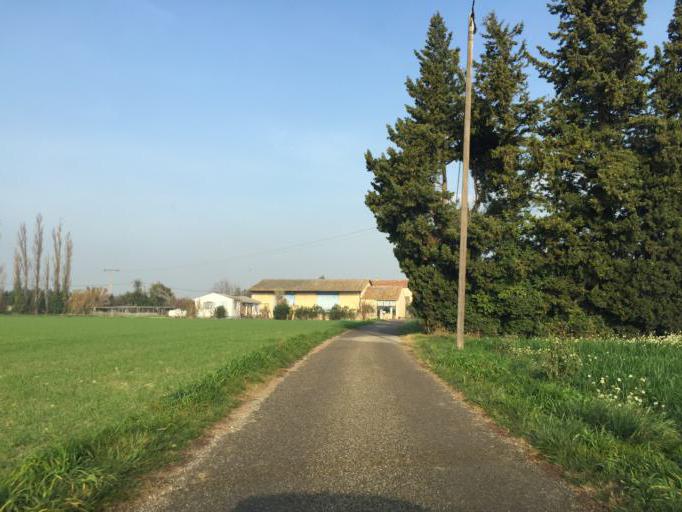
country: FR
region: Provence-Alpes-Cote d'Azur
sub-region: Departement du Vaucluse
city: Bedarrides
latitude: 44.0537
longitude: 4.9068
